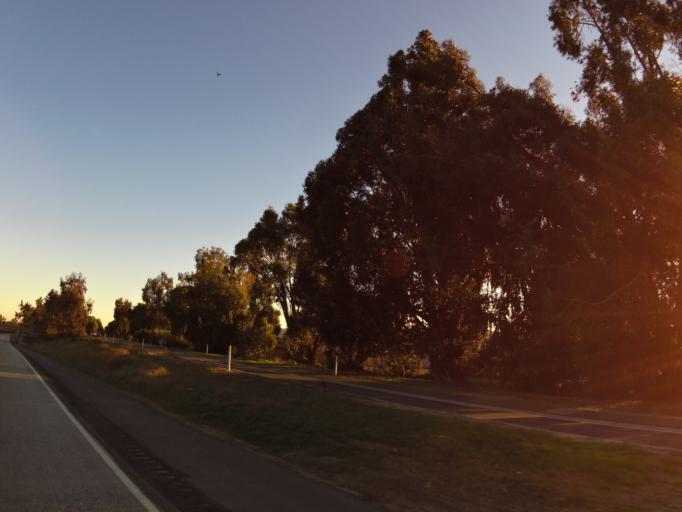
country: US
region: California
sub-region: Monterey County
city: Greenfield
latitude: 36.3257
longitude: -121.2400
